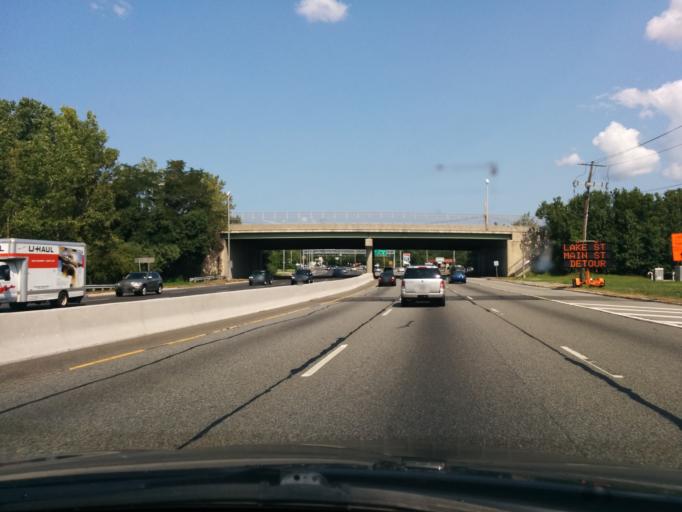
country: US
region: New Jersey
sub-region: Bergen County
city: Ramsey
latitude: 41.0594
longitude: -74.1222
